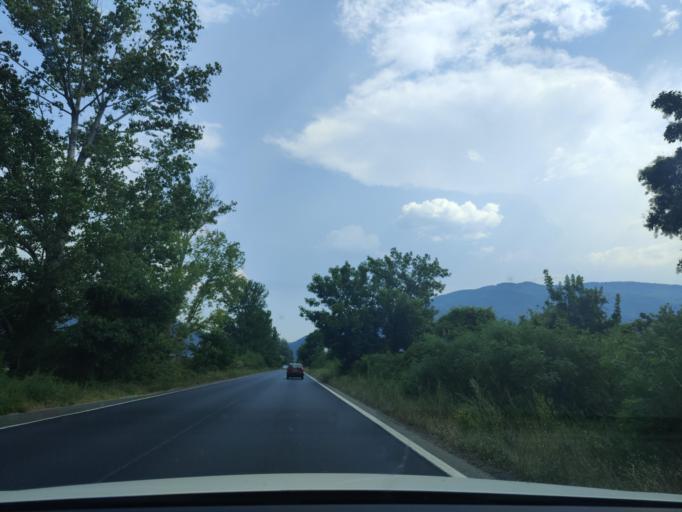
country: BG
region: Blagoevgrad
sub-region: Obshtina Simitli
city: Simitli
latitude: 41.8692
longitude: 23.1255
